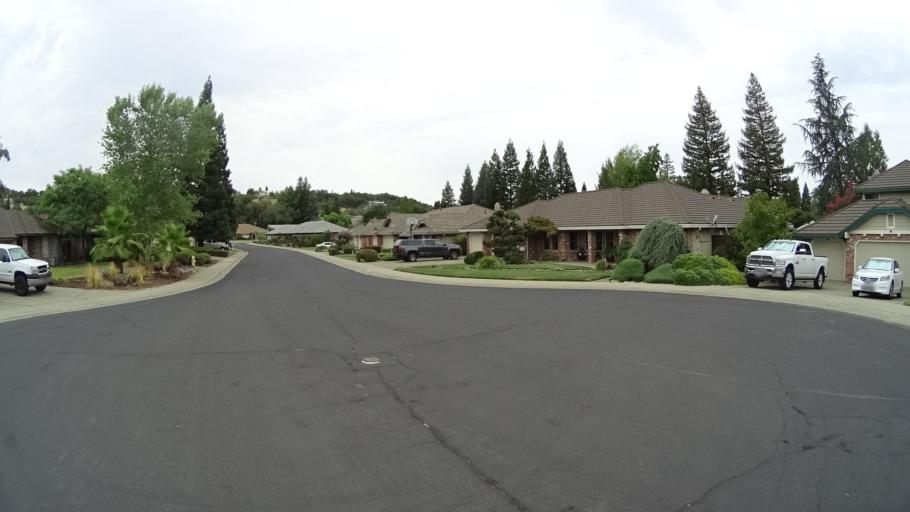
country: US
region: California
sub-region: Placer County
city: Rocklin
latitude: 38.7830
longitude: -121.2126
